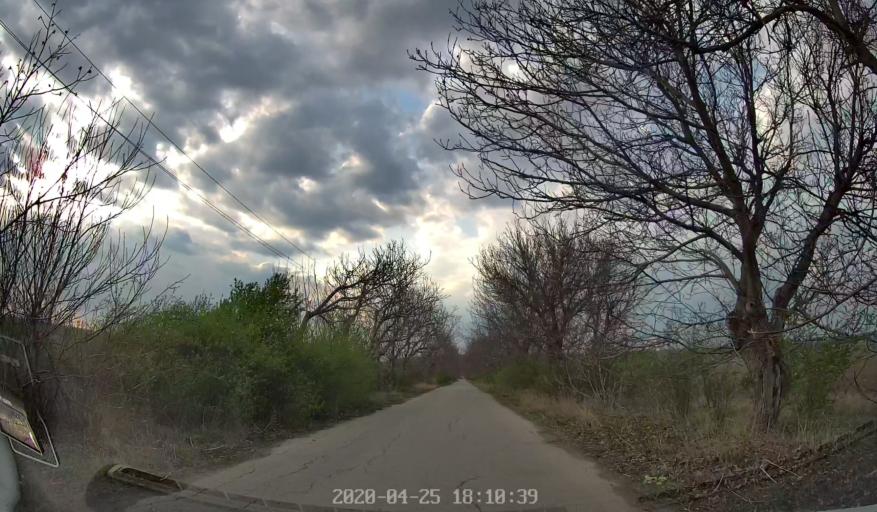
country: MD
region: Chisinau
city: Vadul lui Voda
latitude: 47.1350
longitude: 29.0753
